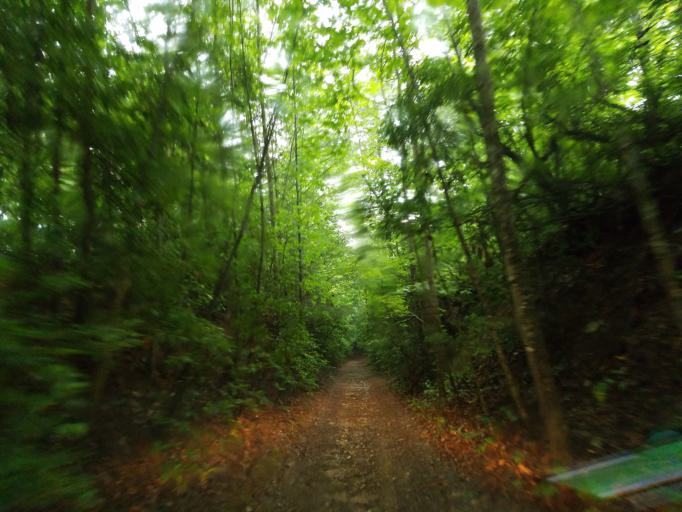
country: US
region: Georgia
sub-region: Lumpkin County
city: Dahlonega
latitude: 34.6911
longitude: -84.0629
